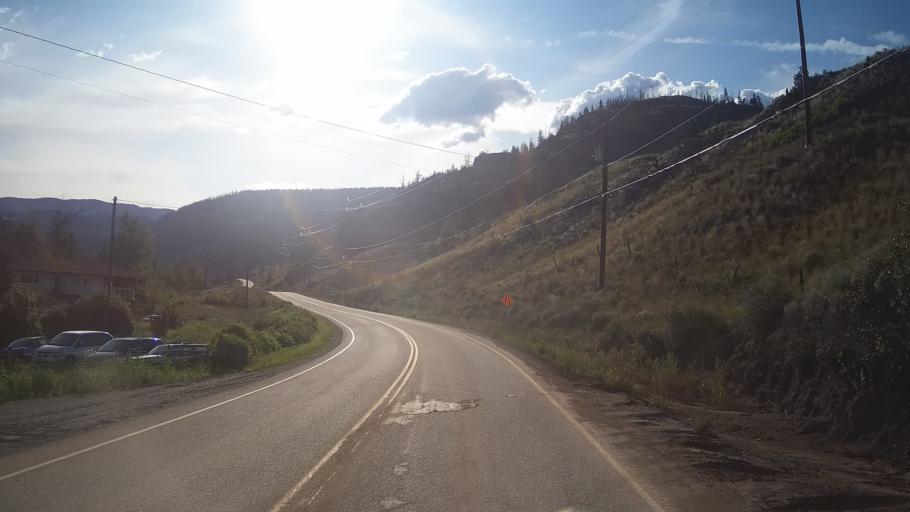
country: CA
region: British Columbia
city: Cache Creek
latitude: 50.8848
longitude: -121.4798
